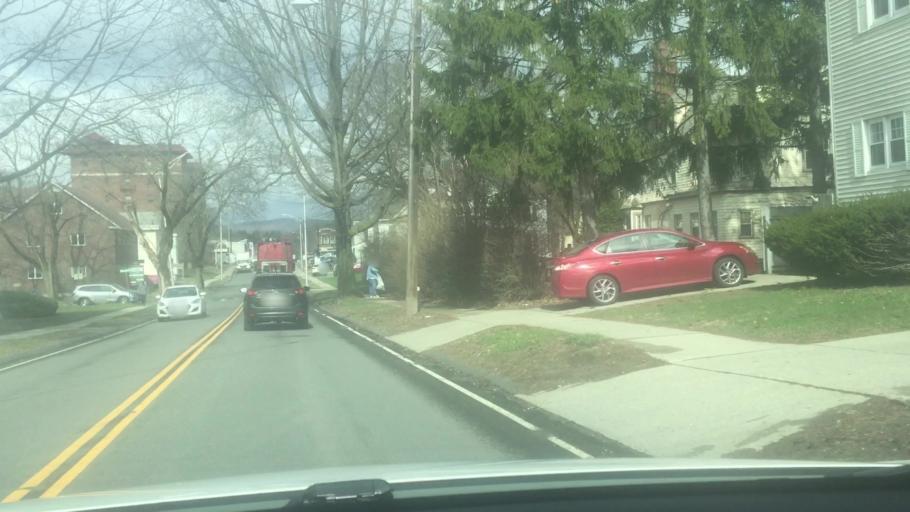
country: US
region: Massachusetts
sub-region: Berkshire County
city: Pittsfield
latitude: 42.4450
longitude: -73.2520
